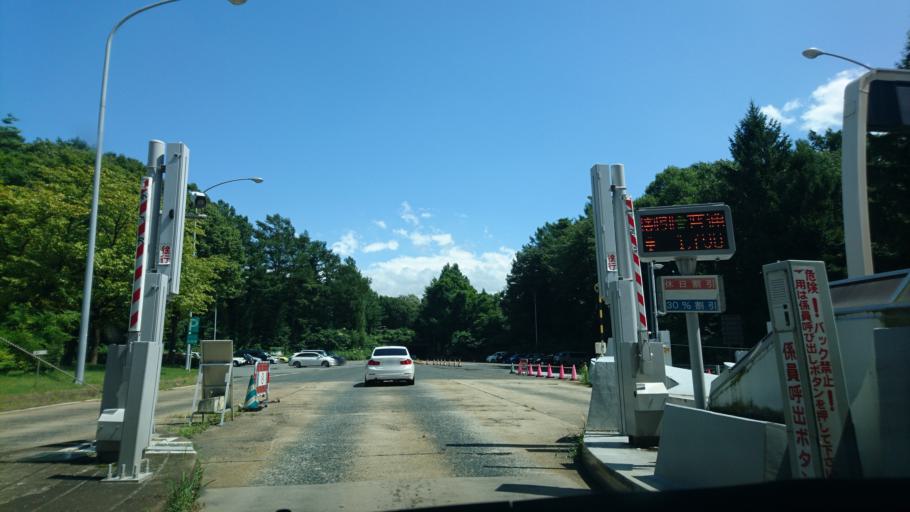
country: JP
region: Iwate
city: Morioka-shi
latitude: 39.7975
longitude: 141.1163
